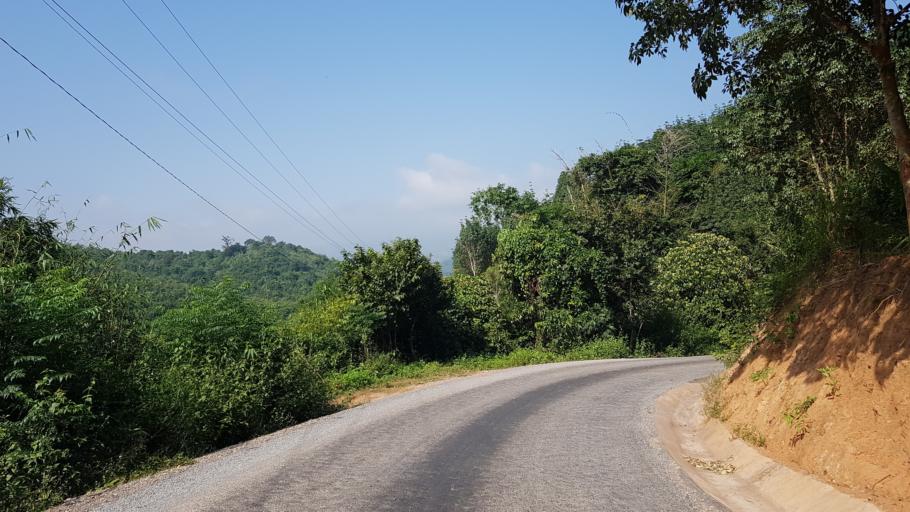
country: LA
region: Oudomxai
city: Muang Xay
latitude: 20.7118
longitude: 102.0558
